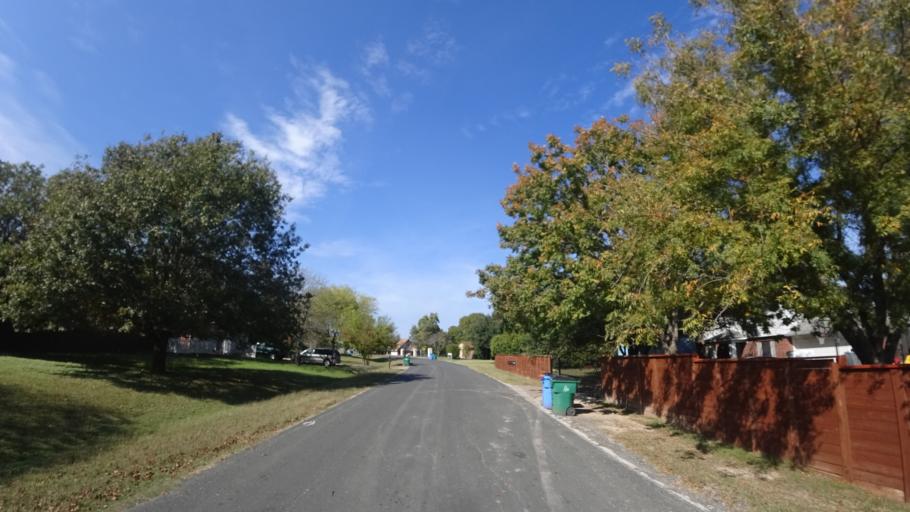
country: US
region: Texas
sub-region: Travis County
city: Pflugerville
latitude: 30.4141
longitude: -97.6285
